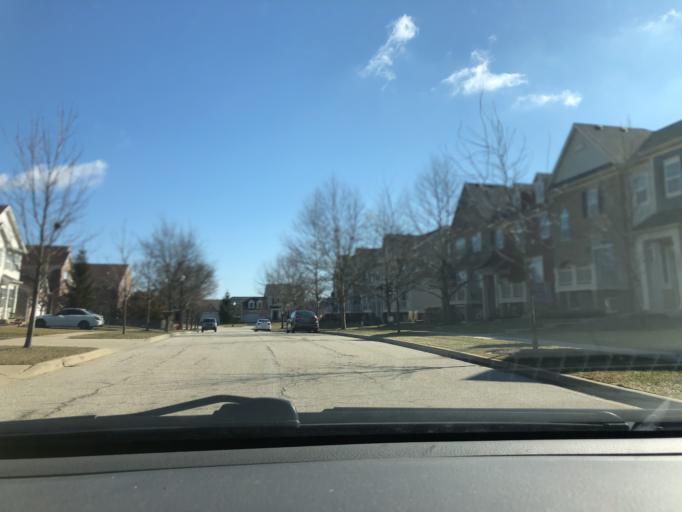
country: US
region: Illinois
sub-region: Kane County
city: Pingree Grove
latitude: 42.0325
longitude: -88.3599
